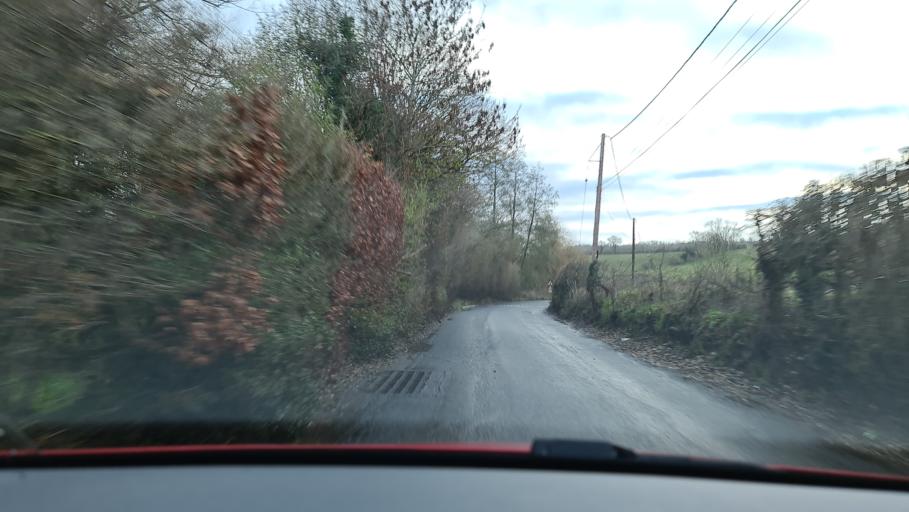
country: GB
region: England
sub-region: Buckinghamshire
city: Chesham
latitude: 51.6873
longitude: -0.5868
